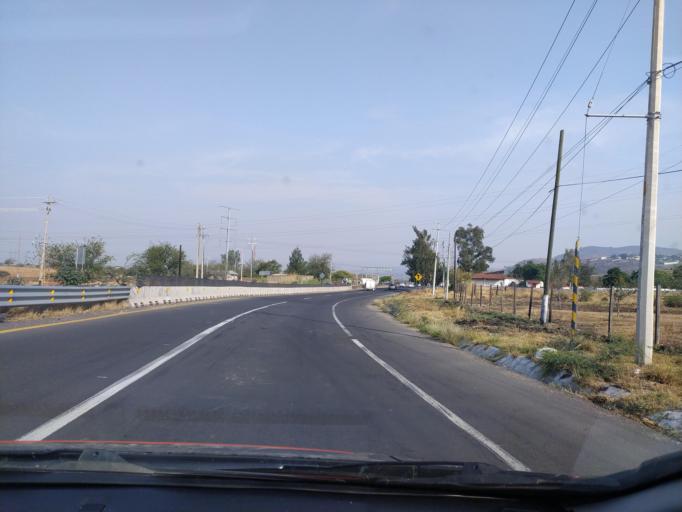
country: MX
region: Jalisco
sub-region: Acatlan de Juarez
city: Villa de los Ninos
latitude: 20.4237
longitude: -103.5575
